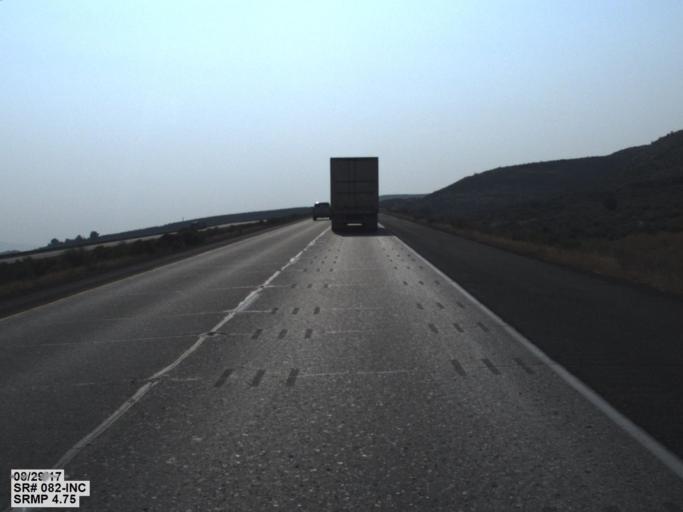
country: US
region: Washington
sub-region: Kittitas County
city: Kittitas
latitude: 46.9125
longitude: -120.4747
